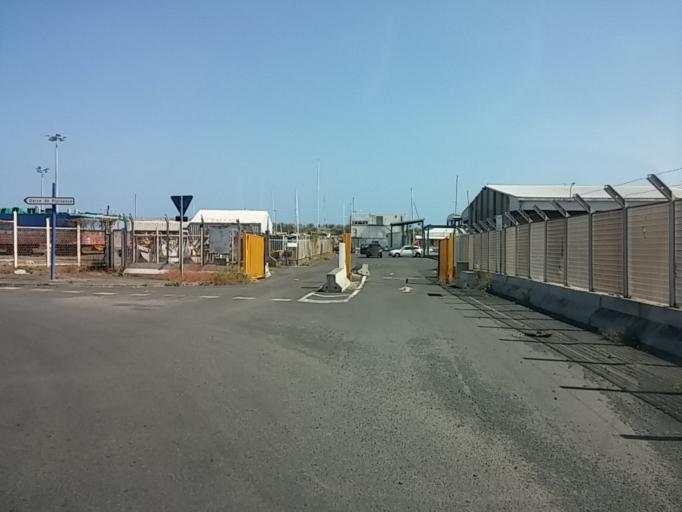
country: RE
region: Reunion
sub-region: Reunion
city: Le Port
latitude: -20.9405
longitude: 55.2849
